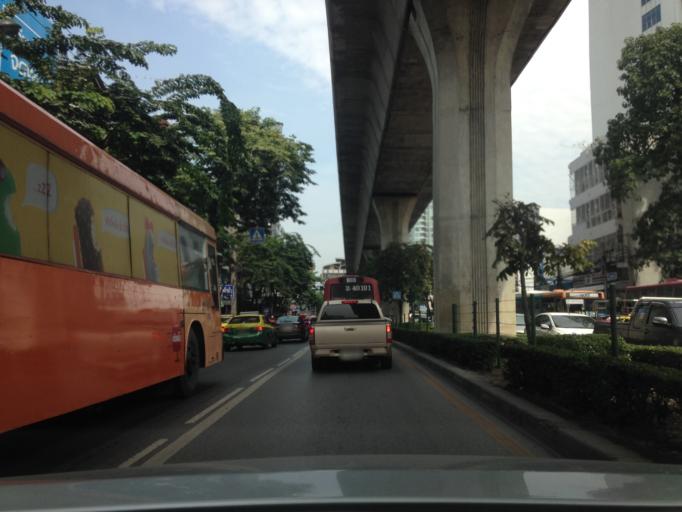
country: TH
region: Bangkok
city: Phaya Thai
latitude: 13.7915
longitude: 100.5489
